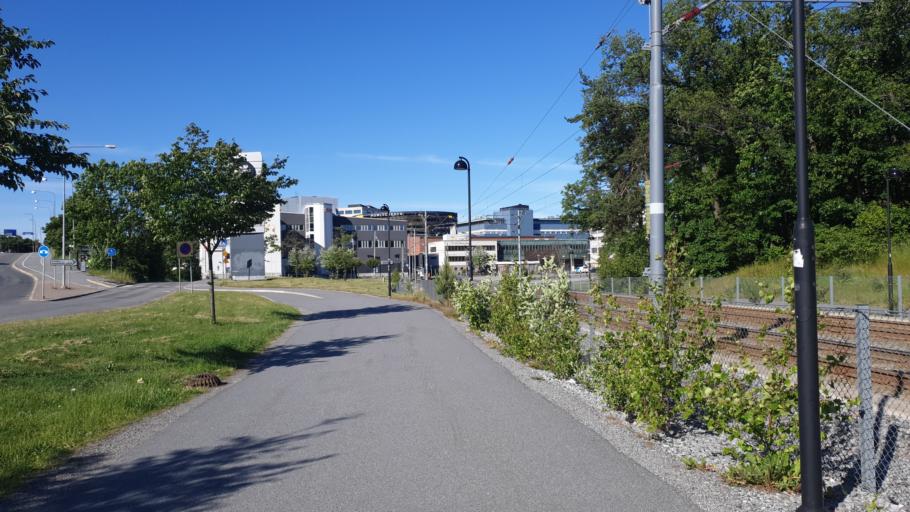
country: SE
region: Stockholm
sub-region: Solna Kommun
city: Rasunda
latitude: 59.3585
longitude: 17.9856
